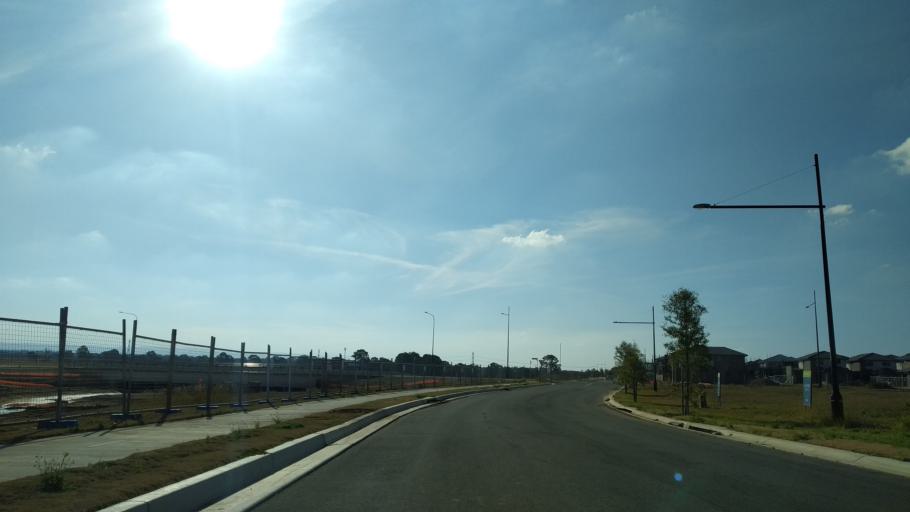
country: AU
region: New South Wales
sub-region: Blacktown
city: Blackett
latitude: -33.6971
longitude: 150.8069
